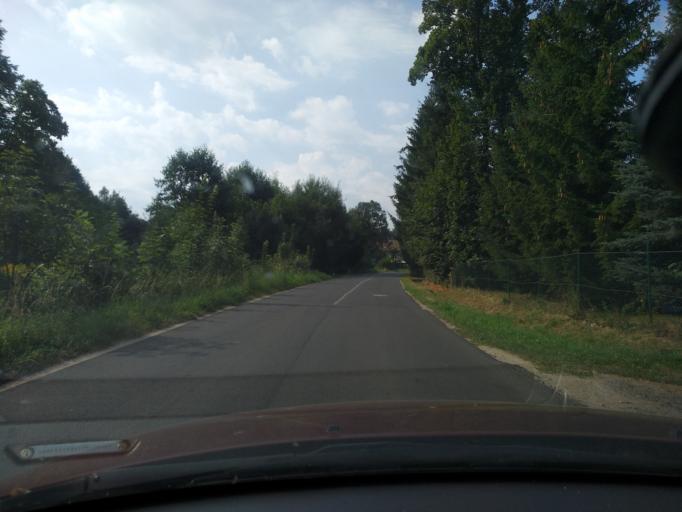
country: PL
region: Lower Silesian Voivodeship
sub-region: Powiat jeleniogorski
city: Stara Kamienica
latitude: 50.9054
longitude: 15.5688
